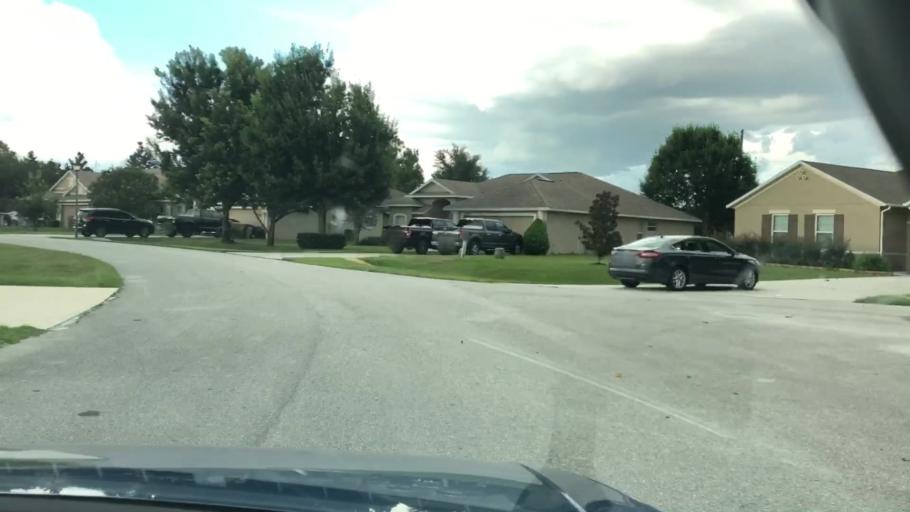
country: US
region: Florida
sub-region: Lake County
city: Eustis
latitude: 28.8781
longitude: -81.7379
